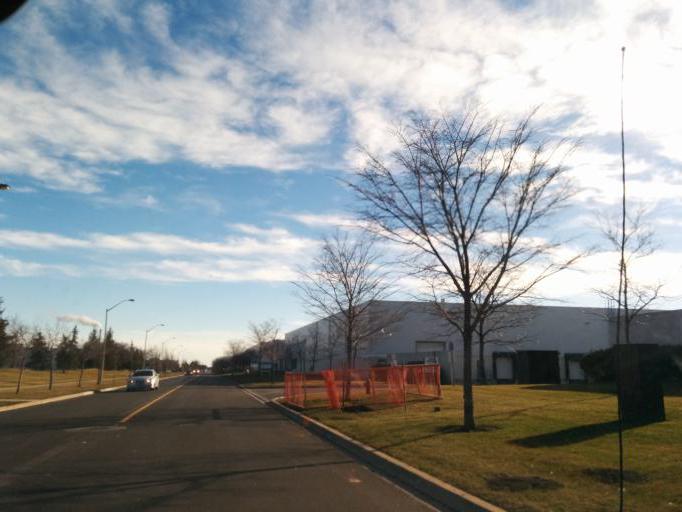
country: CA
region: Ontario
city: Oakville
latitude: 43.5113
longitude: -79.6872
